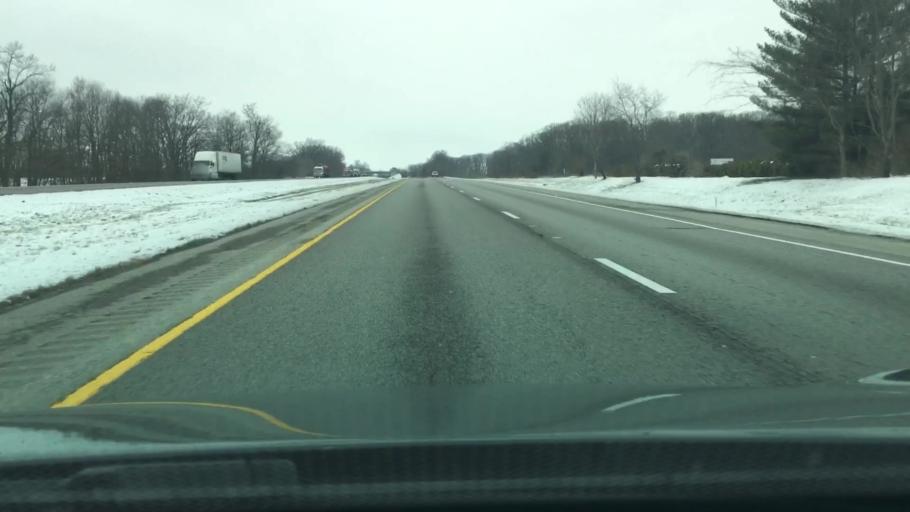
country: US
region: Illinois
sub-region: Clinton County
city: Wamac
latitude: 38.3823
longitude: -89.1176
